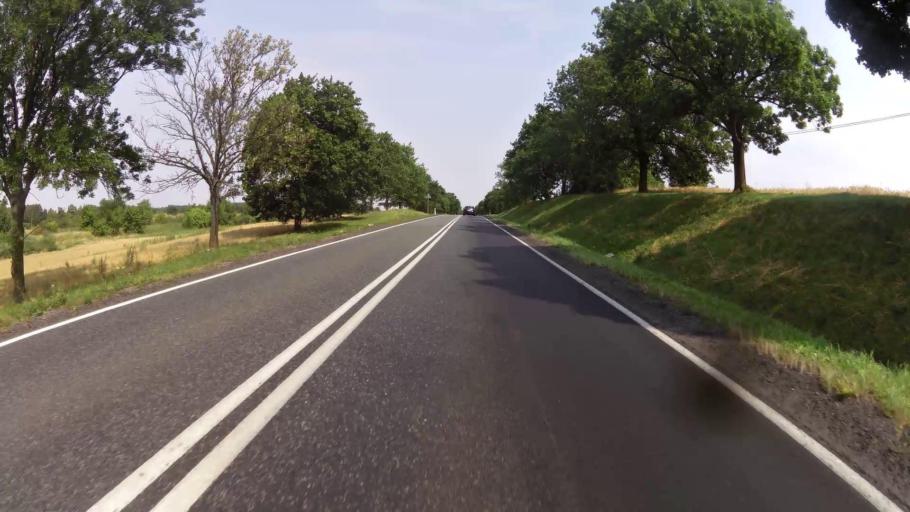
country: PL
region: West Pomeranian Voivodeship
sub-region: Powiat mysliborski
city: Mysliborz
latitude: 52.9335
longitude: 14.8967
